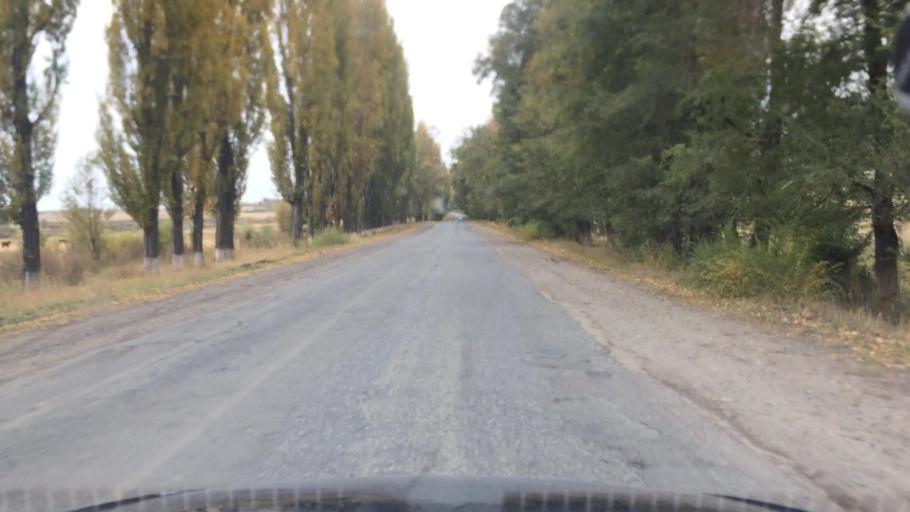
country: KG
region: Ysyk-Koel
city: Pokrovka
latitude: 42.7388
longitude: 77.9149
